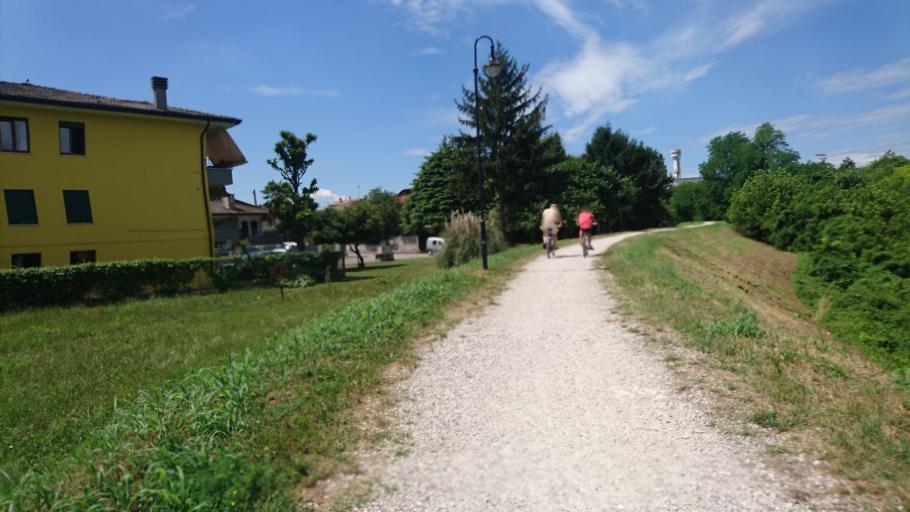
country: IT
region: Veneto
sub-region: Provincia di Padova
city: Padova
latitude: 45.4035
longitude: 11.9077
